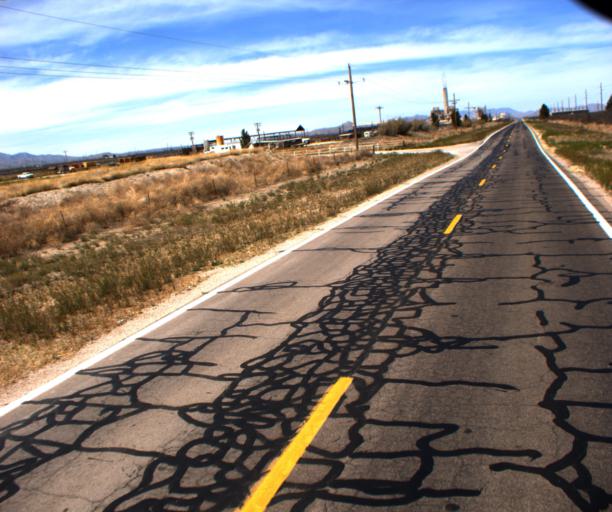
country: US
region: Arizona
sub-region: Cochise County
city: Willcox
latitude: 32.0455
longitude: -109.8837
